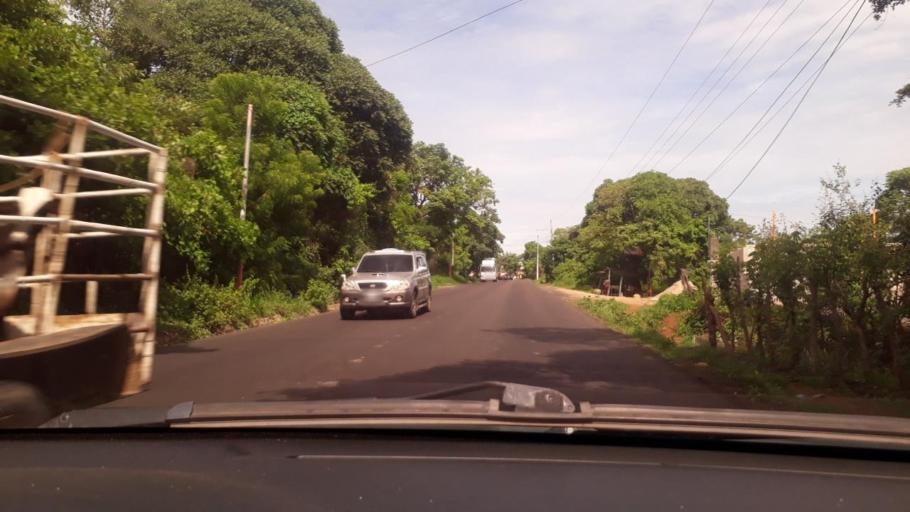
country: GT
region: Jutiapa
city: Quesada
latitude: 14.2710
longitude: -90.0060
